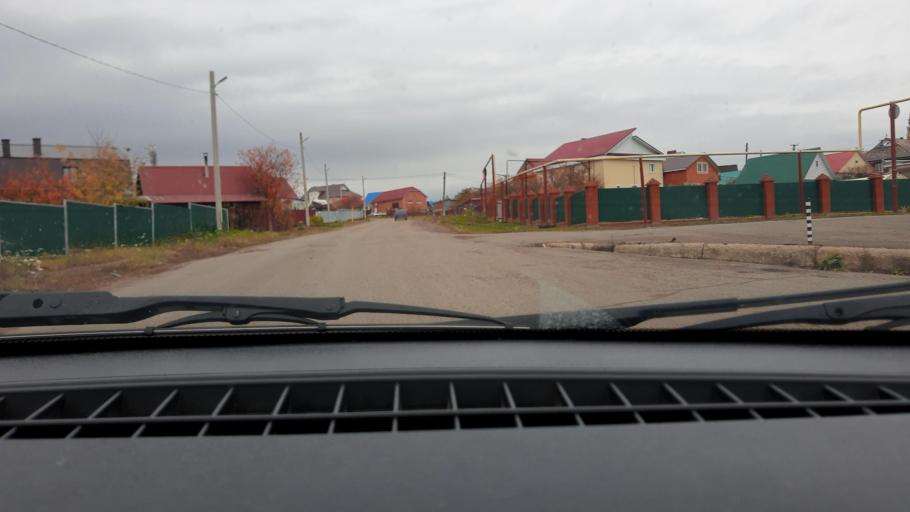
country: RU
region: Bashkortostan
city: Mikhaylovka
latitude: 54.8136
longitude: 55.8936
